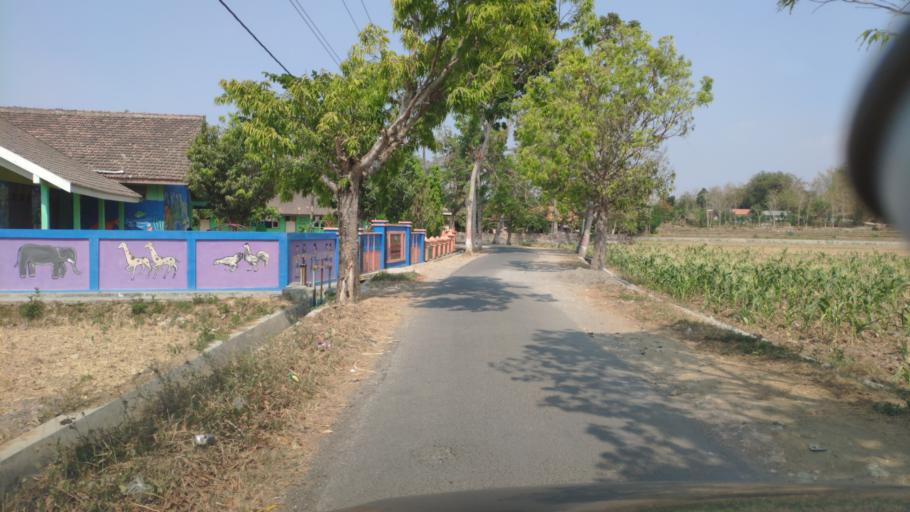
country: ID
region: Central Java
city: Tempuran
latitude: -6.9114
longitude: 111.4581
